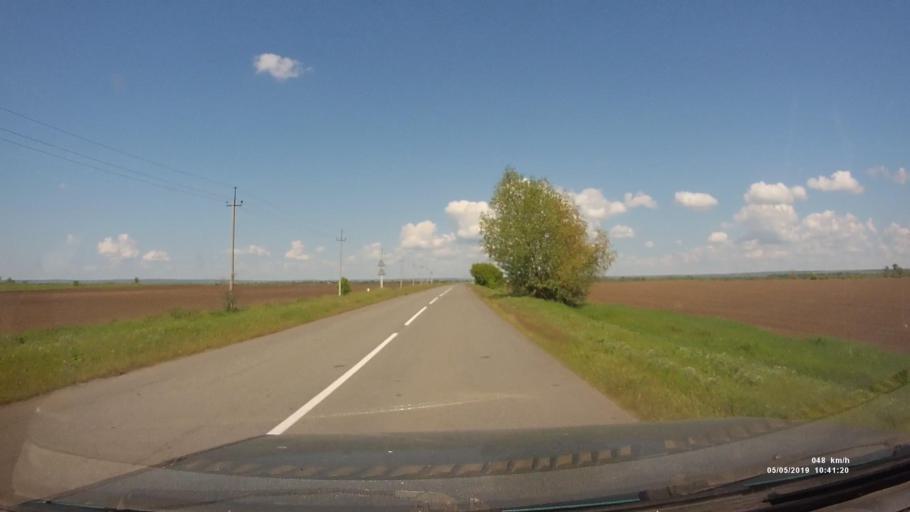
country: RU
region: Rostov
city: Ust'-Donetskiy
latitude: 47.5902
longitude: 40.8431
